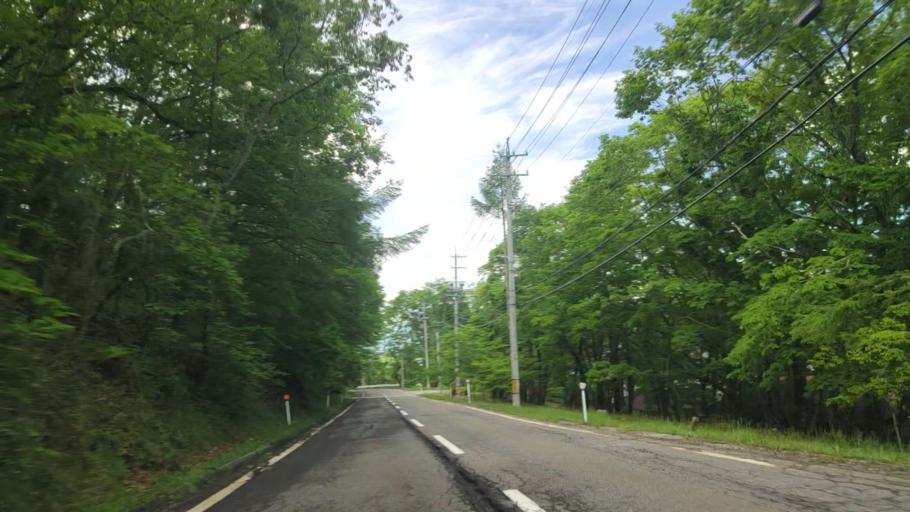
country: JP
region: Nagano
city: Chino
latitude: 36.0666
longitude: 138.2905
